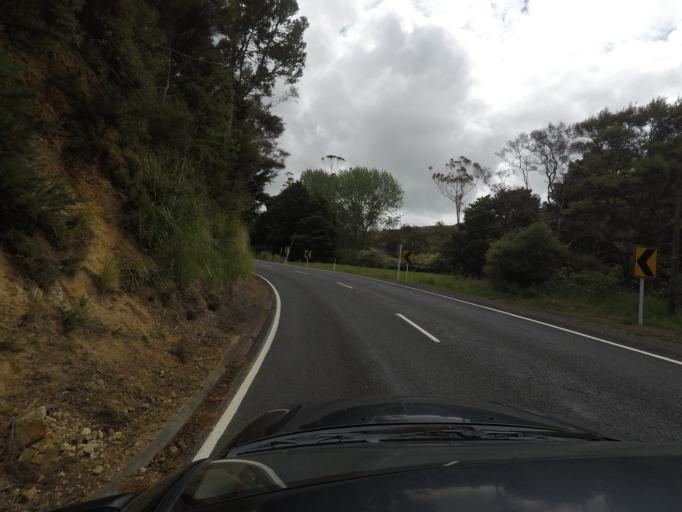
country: NZ
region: Auckland
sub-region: Auckland
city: Parakai
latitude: -36.5026
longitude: 174.4711
